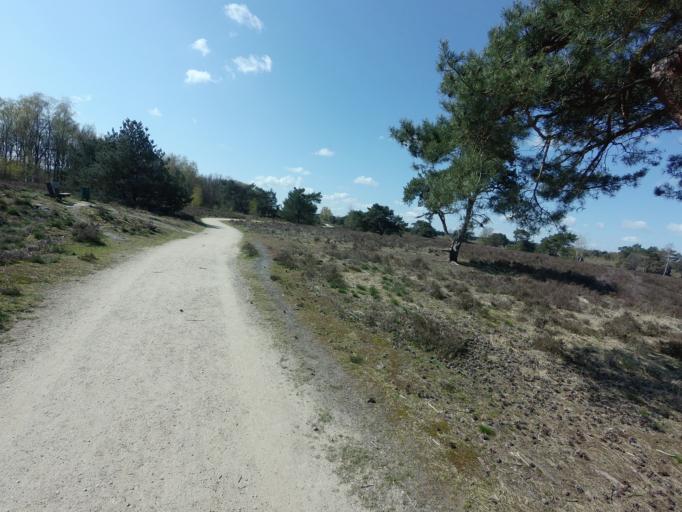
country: NL
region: Limburg
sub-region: Gemeente Bergen
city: Wellerlooi
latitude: 51.6105
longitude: 6.0732
